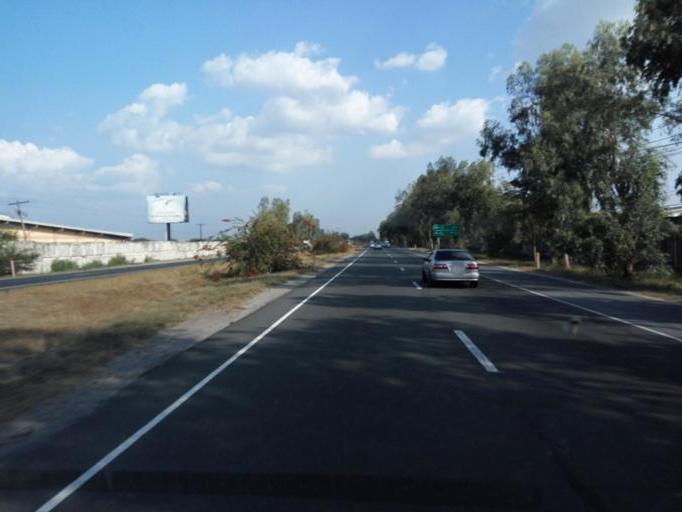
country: PH
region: Central Luzon
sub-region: Province of Pampanga
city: Balibago
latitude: 15.1542
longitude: 120.6198
